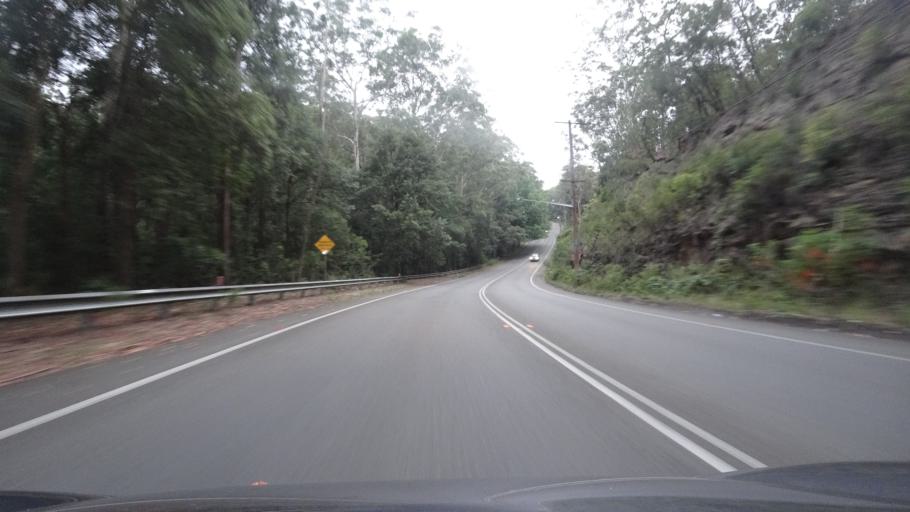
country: AU
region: New South Wales
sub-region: Ku-ring-gai
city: Normanhurst
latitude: -33.7398
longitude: 151.1055
